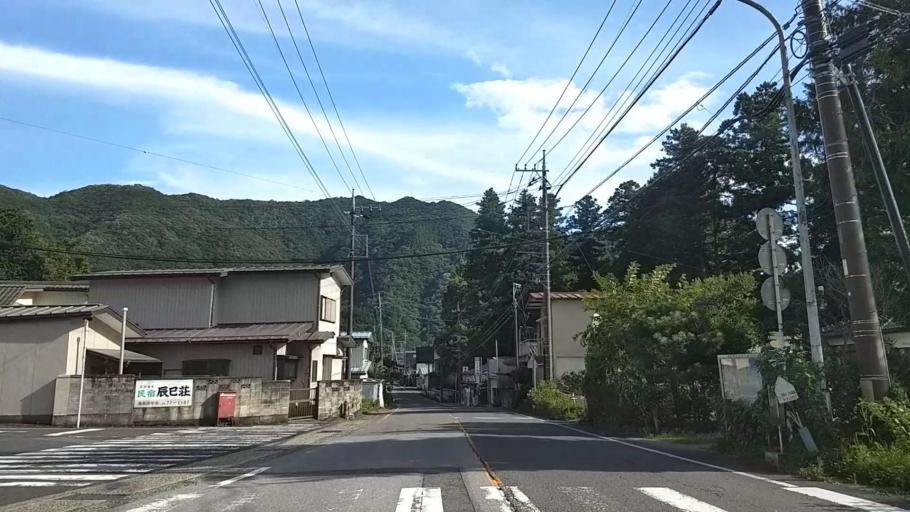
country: JP
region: Tochigi
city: Imaichi
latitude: 36.8561
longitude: 139.7296
